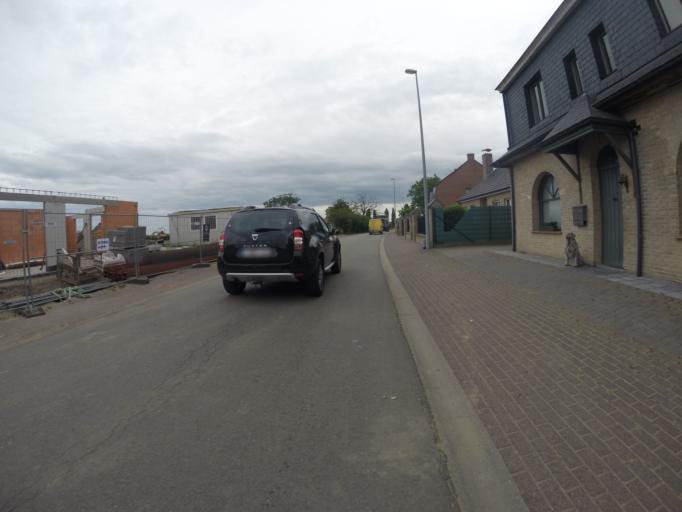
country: BE
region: Flanders
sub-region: Provincie West-Vlaanderen
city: Ruiselede
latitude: 51.0683
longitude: 3.3577
